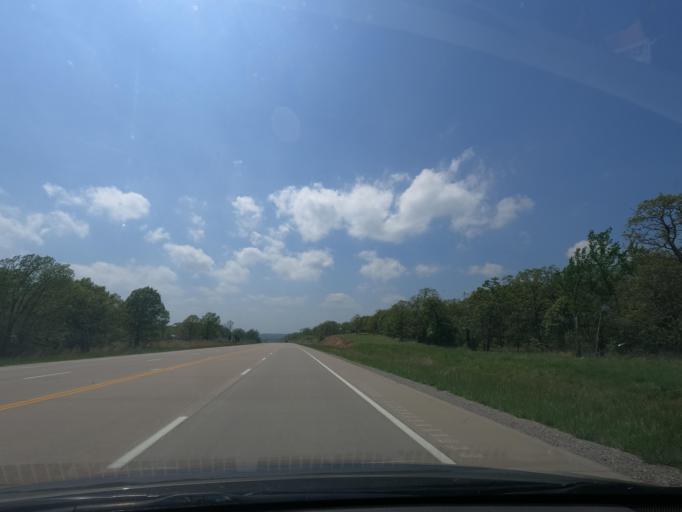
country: US
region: Kansas
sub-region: Wilson County
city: Fredonia
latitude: 37.6142
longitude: -95.9172
